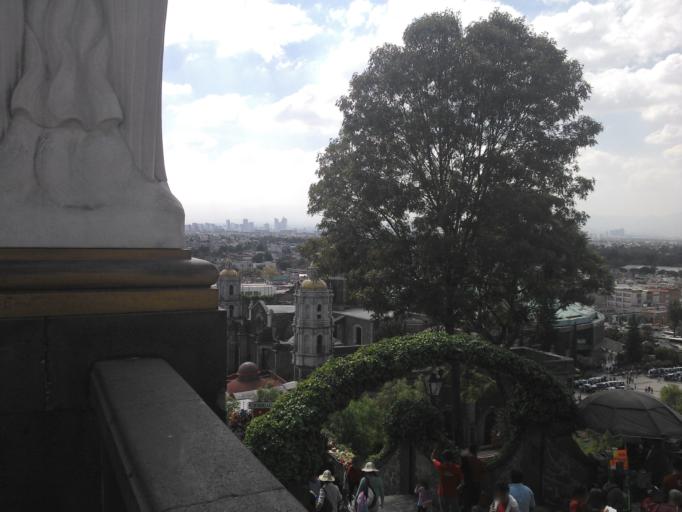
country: MX
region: Mexico City
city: Gustavo A. Madero
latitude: 19.4859
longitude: -99.1161
